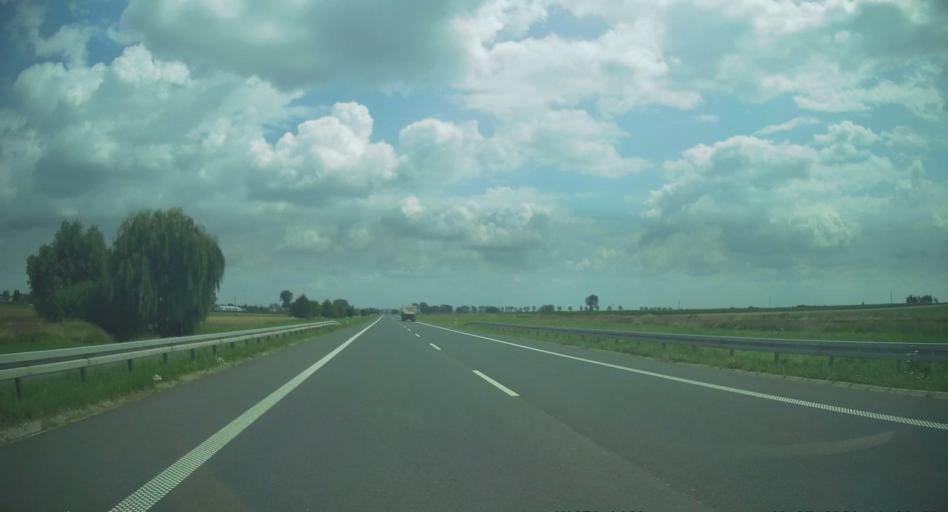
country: PL
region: Opole Voivodeship
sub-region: Powiat prudnicki
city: Lubrza
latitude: 50.3289
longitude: 17.6234
